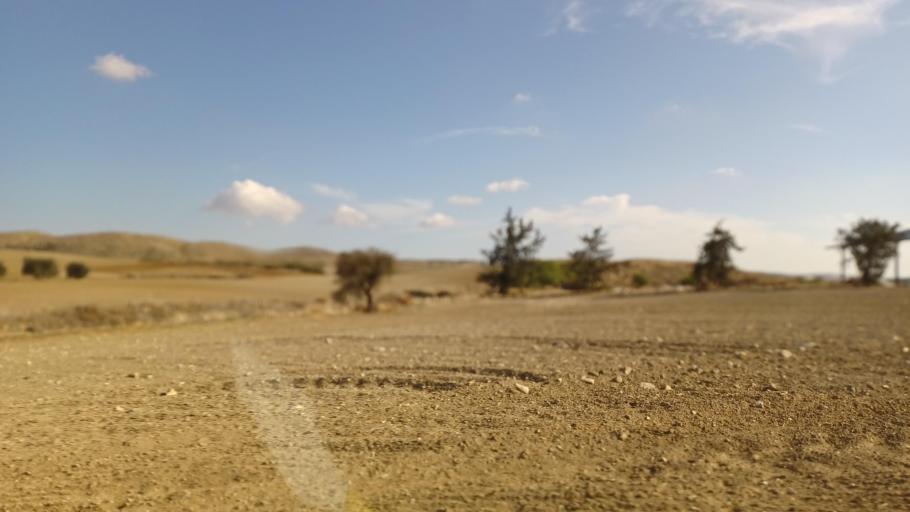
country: CY
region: Larnaka
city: Troulloi
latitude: 35.0200
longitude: 33.5860
